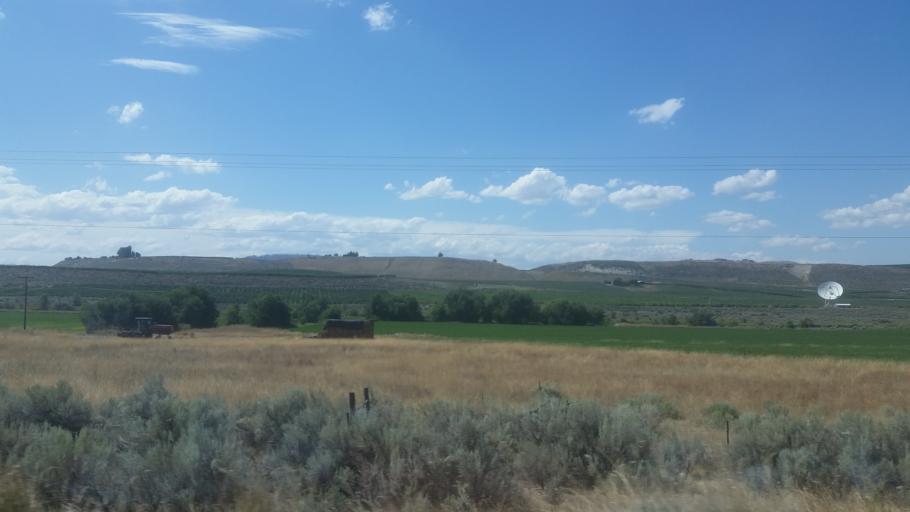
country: US
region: Washington
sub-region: Okanogan County
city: Brewster
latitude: 48.1262
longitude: -119.6734
